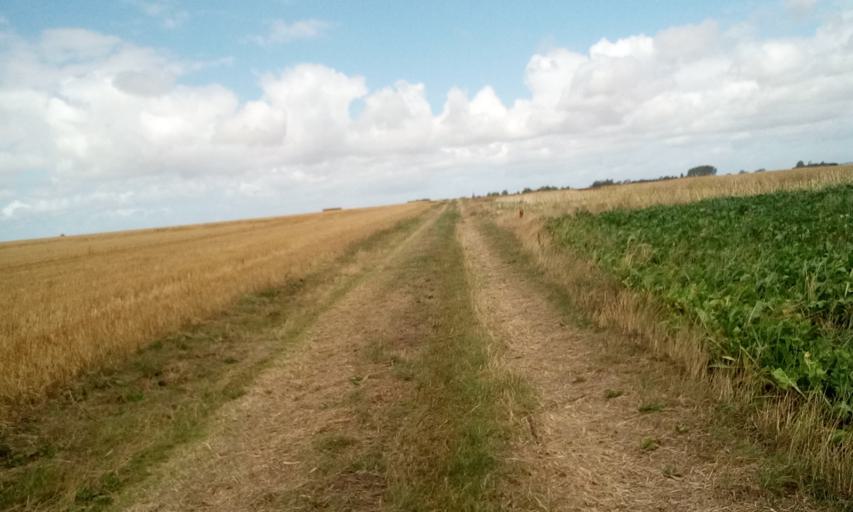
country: FR
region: Lower Normandy
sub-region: Departement du Calvados
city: Cheux
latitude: 49.1758
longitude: -0.5550
